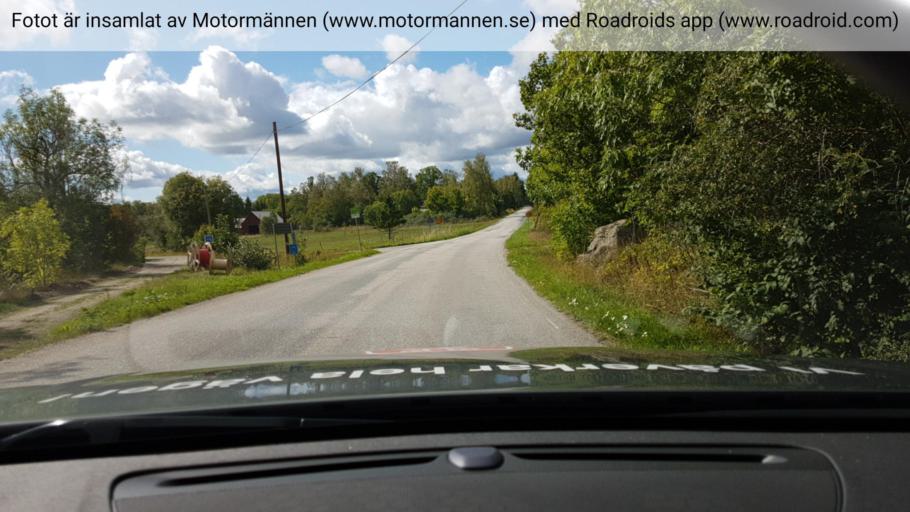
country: SE
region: Soedermanland
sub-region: Strangnas Kommun
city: Stallarholmen
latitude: 59.3734
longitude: 17.2540
